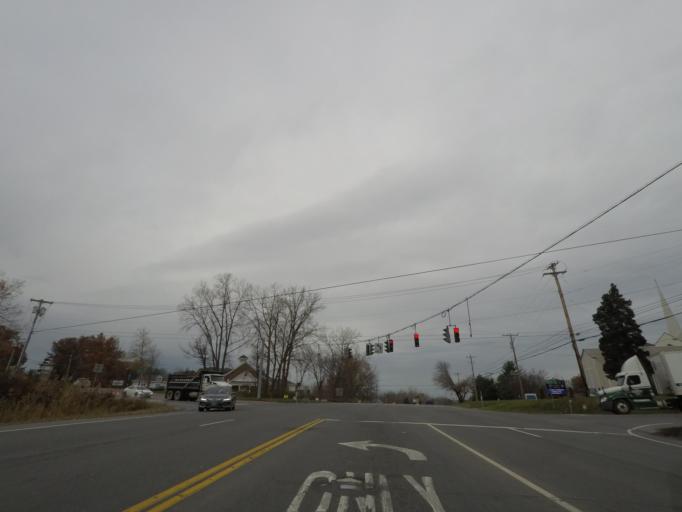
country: US
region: New York
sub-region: Saratoga County
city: Country Knolls
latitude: 42.9050
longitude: -73.7778
